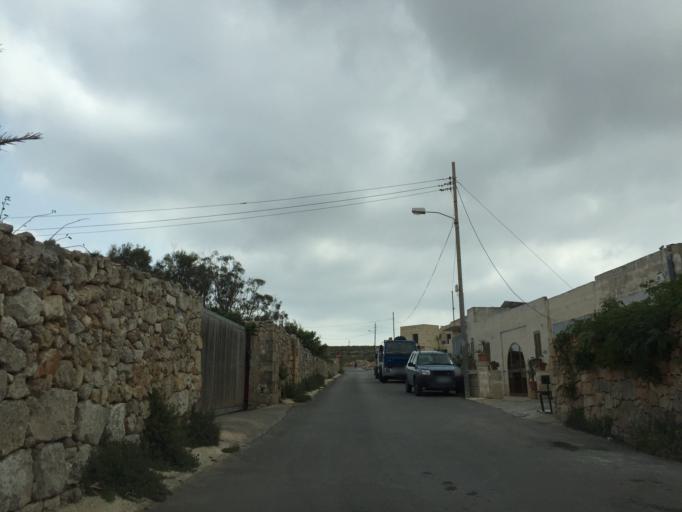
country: MT
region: L-Imtarfa
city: Imtarfa
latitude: 35.9011
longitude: 14.3794
